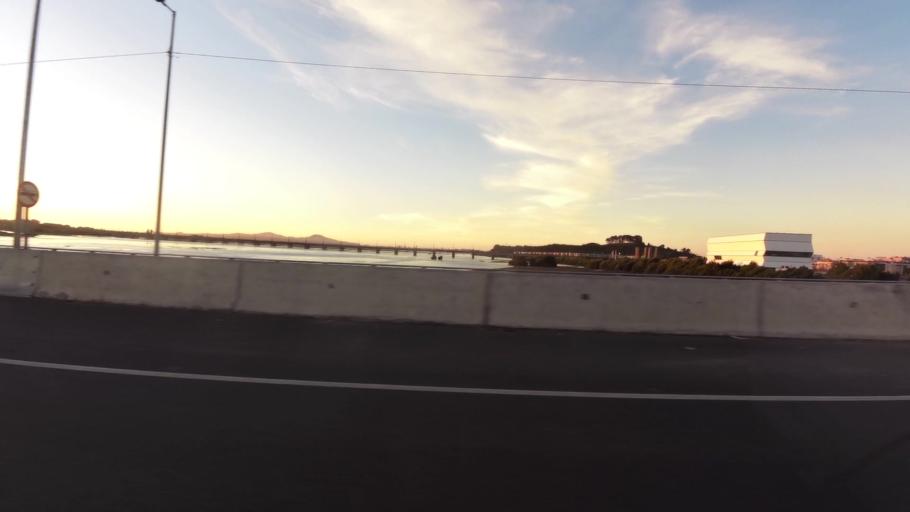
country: CL
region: Biobio
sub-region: Provincia de Concepcion
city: Concepcion
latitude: -36.8375
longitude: -73.0646
